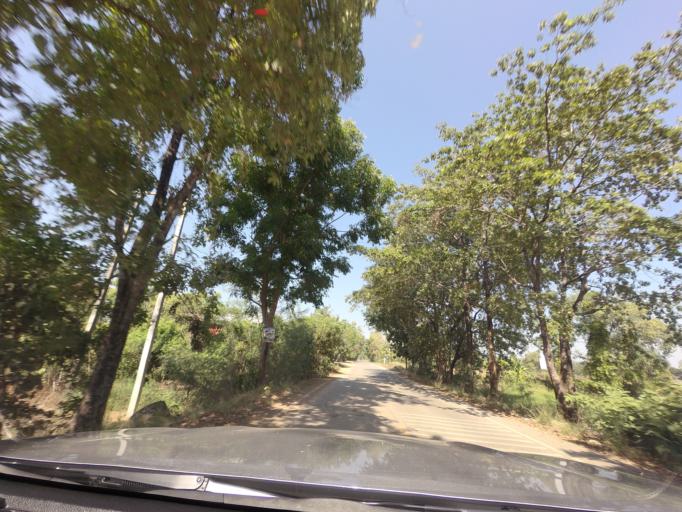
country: TH
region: Sukhothai
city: Si Samrong
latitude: 17.1357
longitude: 99.7715
